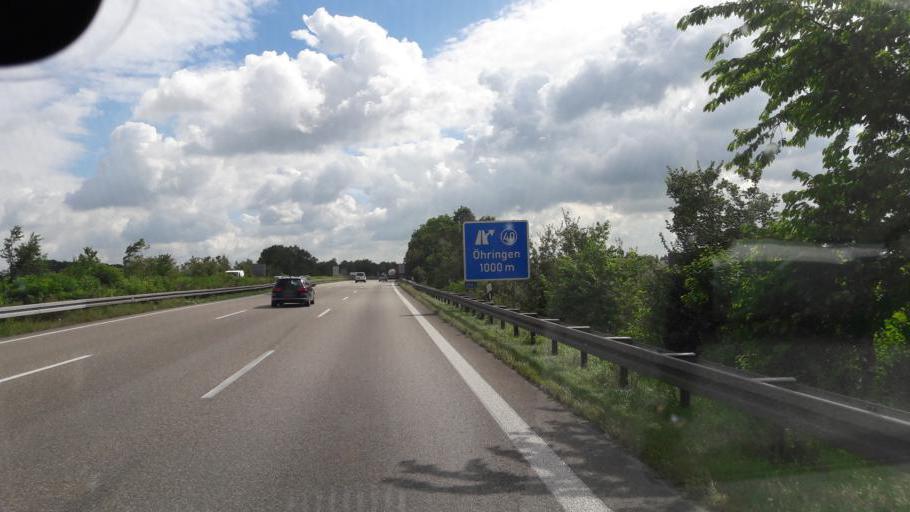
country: DE
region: Baden-Wuerttemberg
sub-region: Regierungsbezirk Stuttgart
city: Bretzfeld
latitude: 49.2013
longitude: 9.4646
